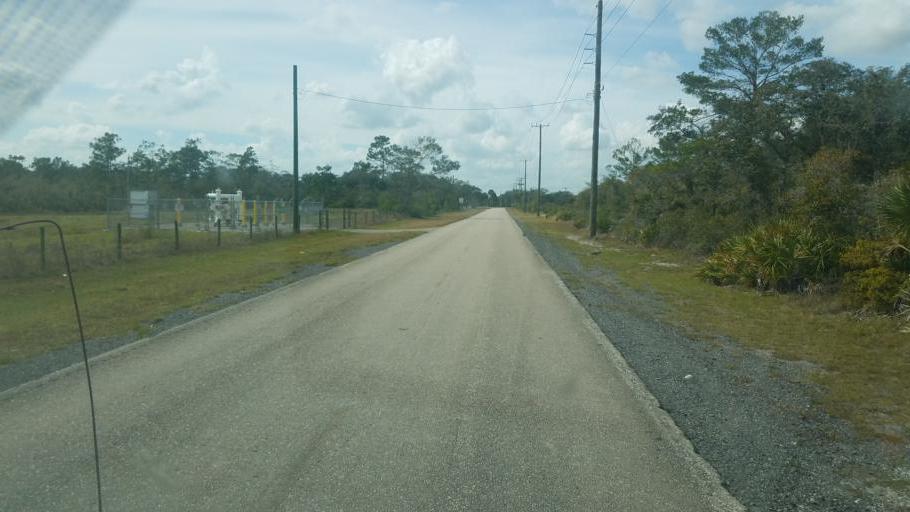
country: US
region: Florida
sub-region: Okeechobee County
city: Cypress Quarters
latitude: 27.5231
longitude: -80.8030
